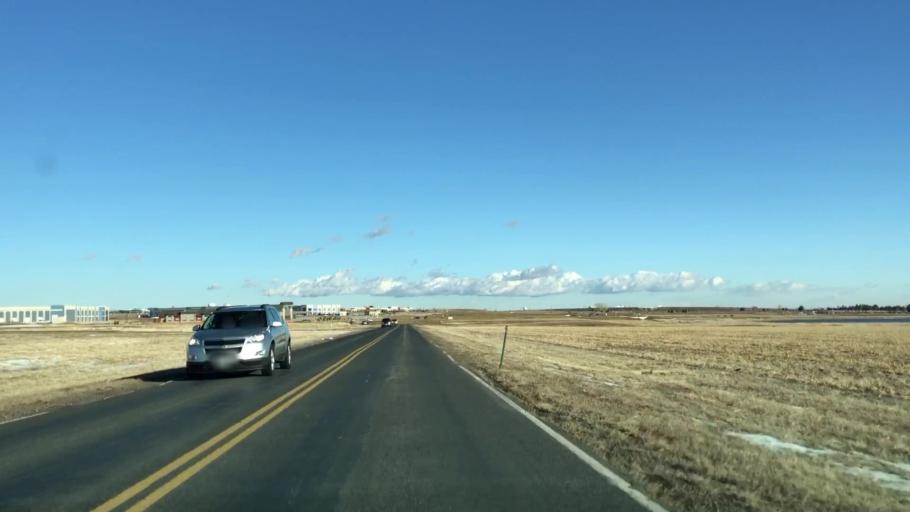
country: US
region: Colorado
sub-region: Larimer County
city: Loveland
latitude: 40.4289
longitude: -105.0170
